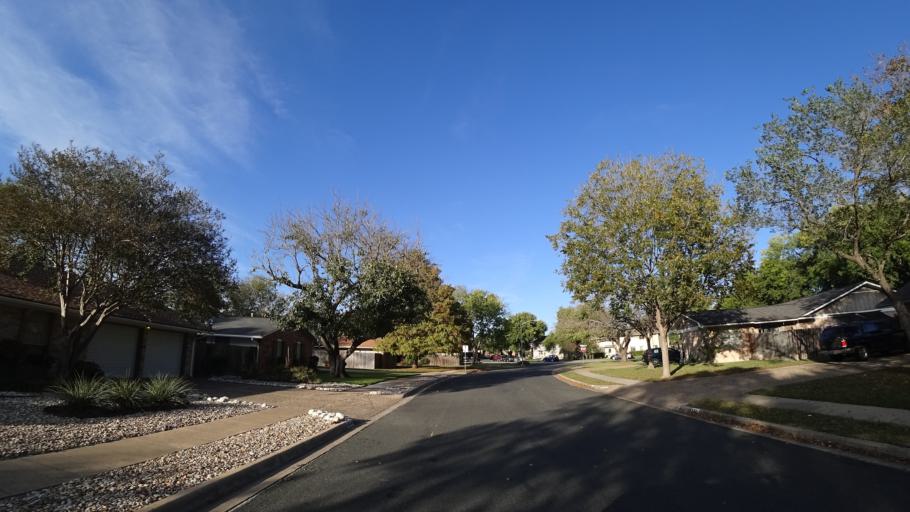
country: US
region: Texas
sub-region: Williamson County
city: Jollyville
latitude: 30.3739
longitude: -97.7349
